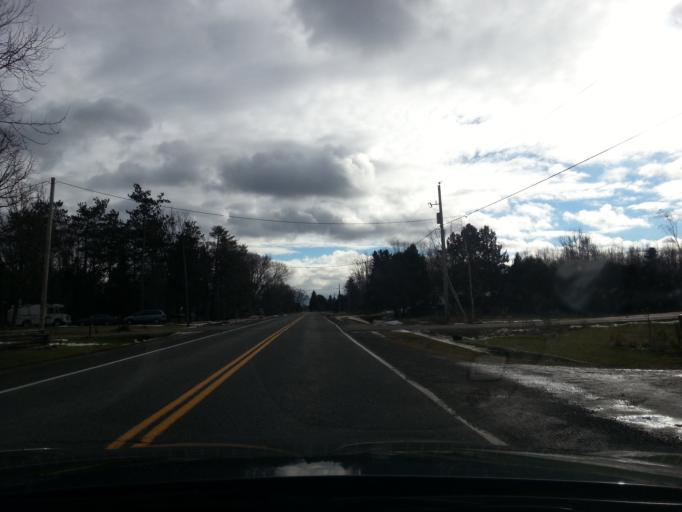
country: CA
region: Ontario
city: Bells Corners
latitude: 45.1096
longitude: -75.6240
